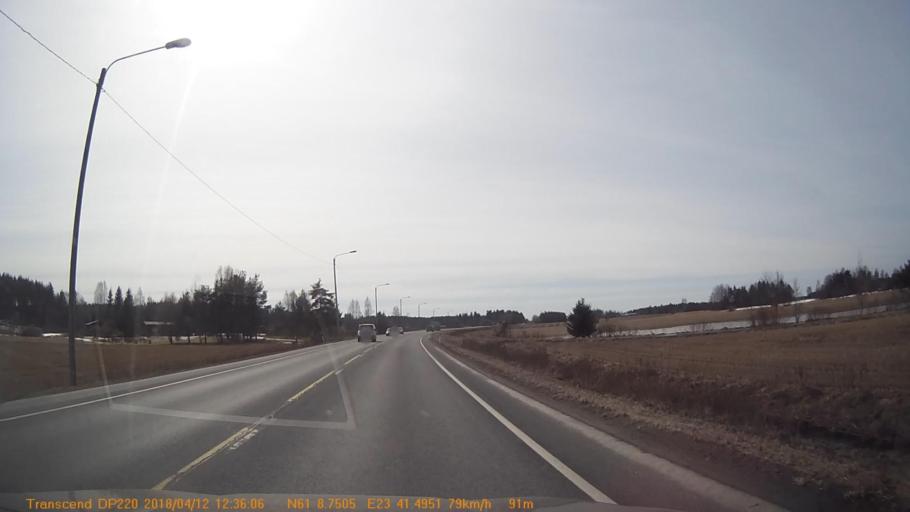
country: FI
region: Pirkanmaa
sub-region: Etelae-Pirkanmaa
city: Kylmaekoski
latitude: 61.1460
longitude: 23.6917
